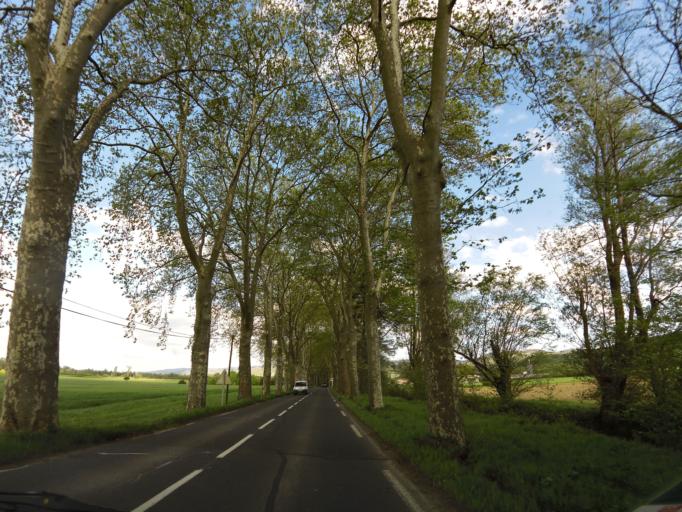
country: FR
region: Midi-Pyrenees
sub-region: Departement de la Haute-Garonne
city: Revel
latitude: 43.4535
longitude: 2.0208
